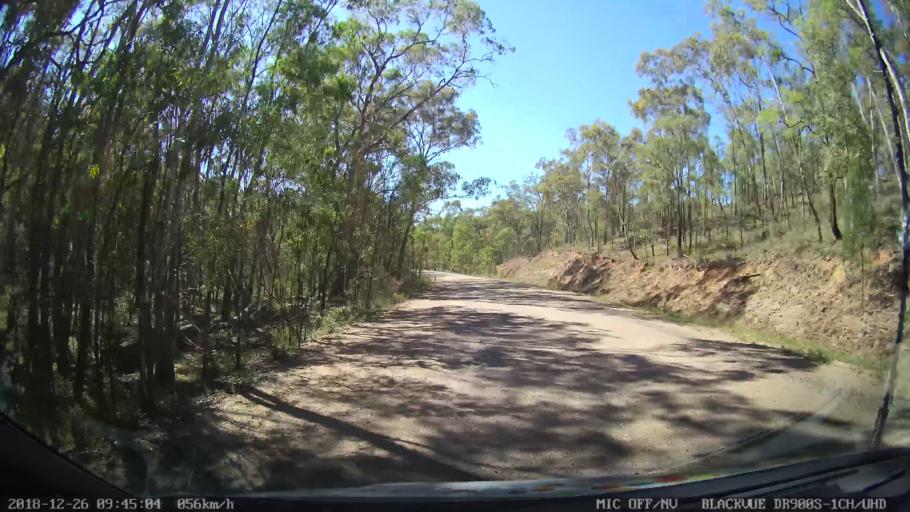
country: AU
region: New South Wales
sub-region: Mid-Western Regional
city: Kandos
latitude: -32.9608
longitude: 150.1005
